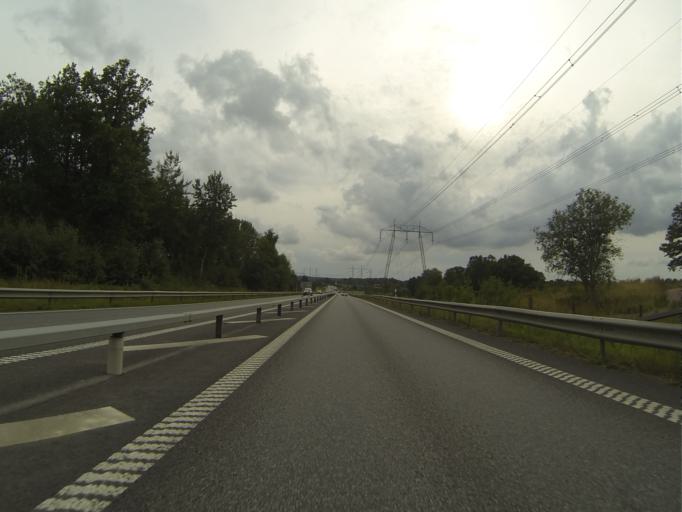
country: SE
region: Skane
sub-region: Horby Kommun
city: Hoerby
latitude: 55.8630
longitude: 13.6480
